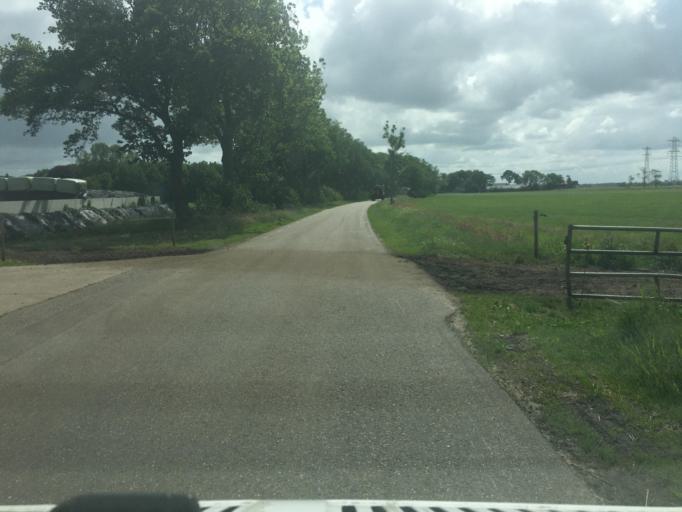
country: NL
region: Friesland
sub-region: Gemeente Heerenveen
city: Oudeschoot
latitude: 52.9237
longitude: 5.9243
